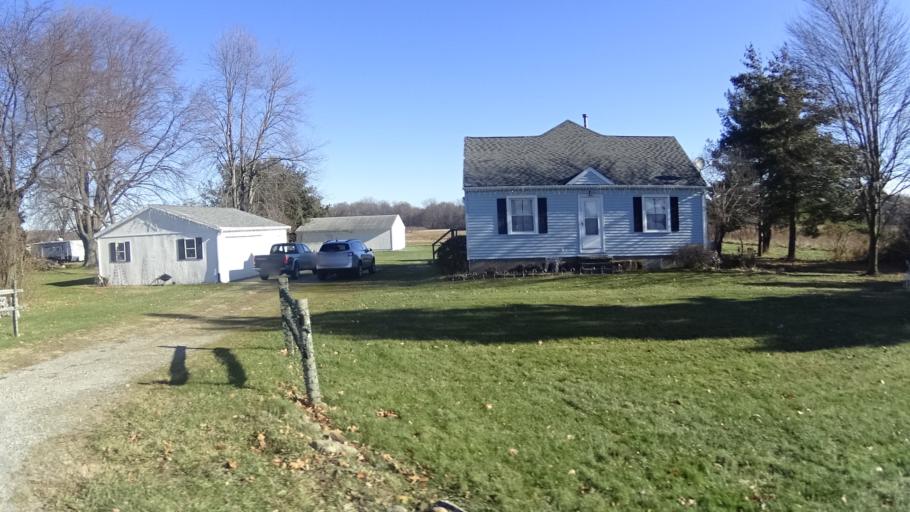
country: US
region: Ohio
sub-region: Lorain County
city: Vermilion-on-the-Lake
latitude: 41.3788
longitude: -82.3103
